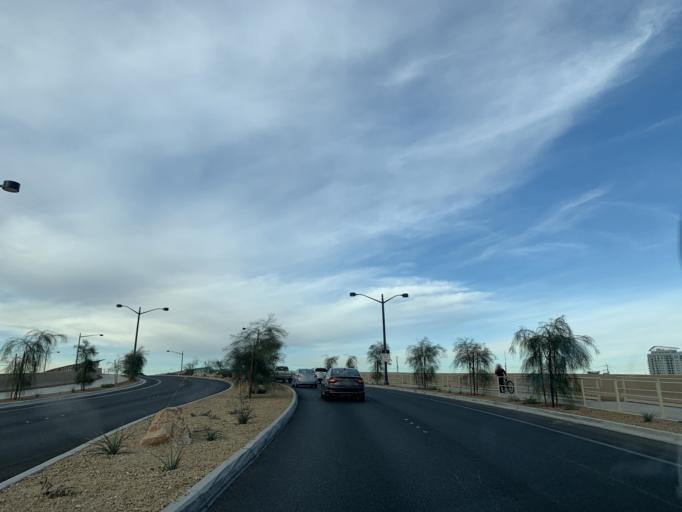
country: US
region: Nevada
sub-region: Clark County
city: Las Vegas
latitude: 36.1543
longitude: -115.1582
